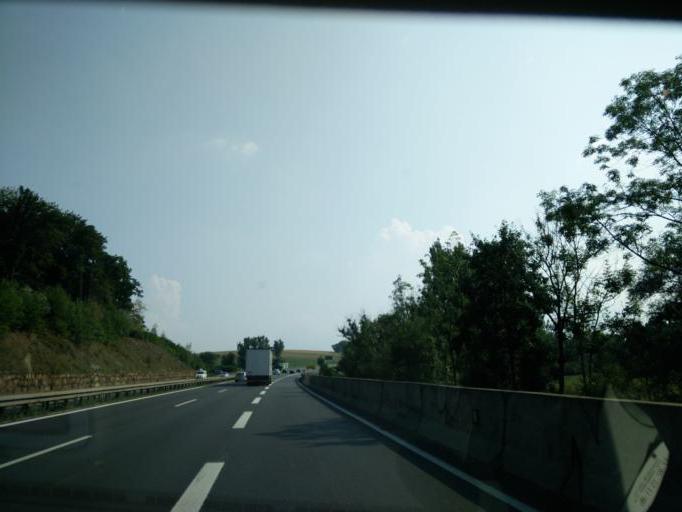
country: DE
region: Baden-Wuerttemberg
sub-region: Tuebingen Region
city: Dusslingen
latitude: 48.4739
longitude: 9.0651
